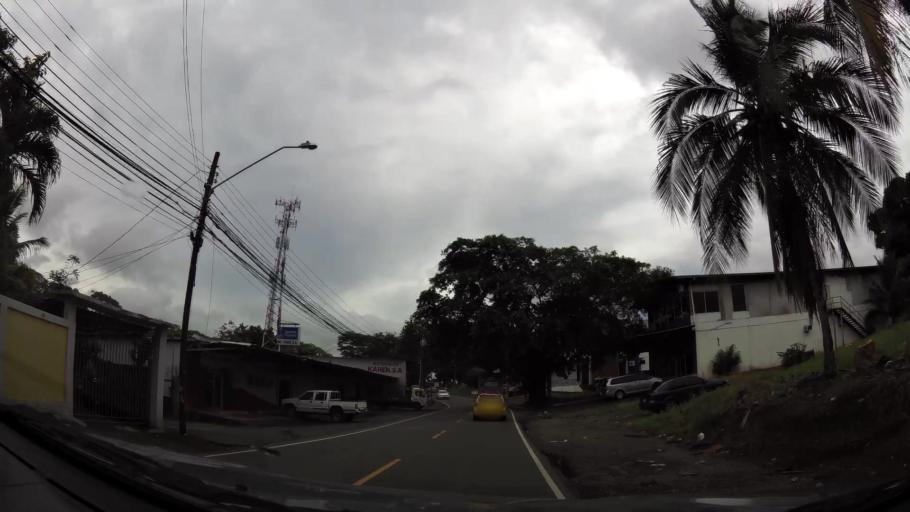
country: PA
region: Chiriqui
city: David
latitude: 8.4347
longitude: -82.4205
